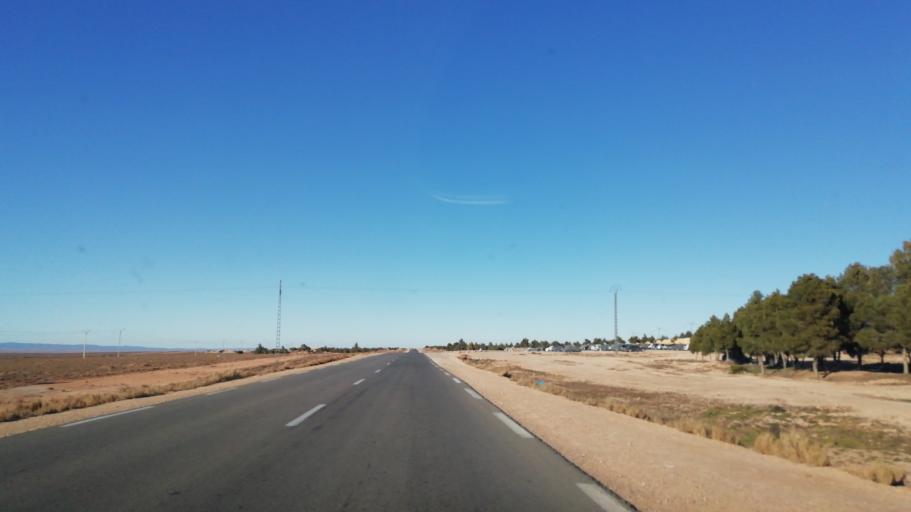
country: DZ
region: Tlemcen
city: Sebdou
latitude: 34.2663
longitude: -1.2582
